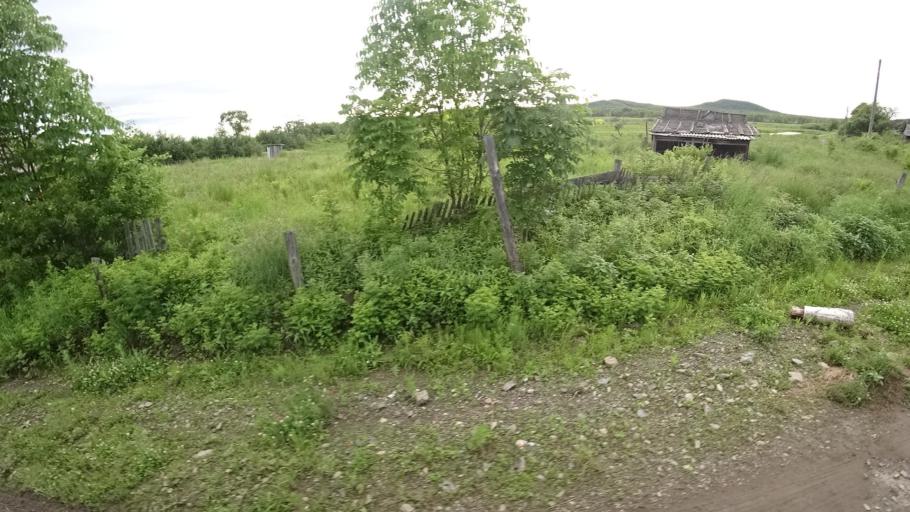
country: RU
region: Khabarovsk Krai
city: Amursk
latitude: 49.8830
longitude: 136.1278
